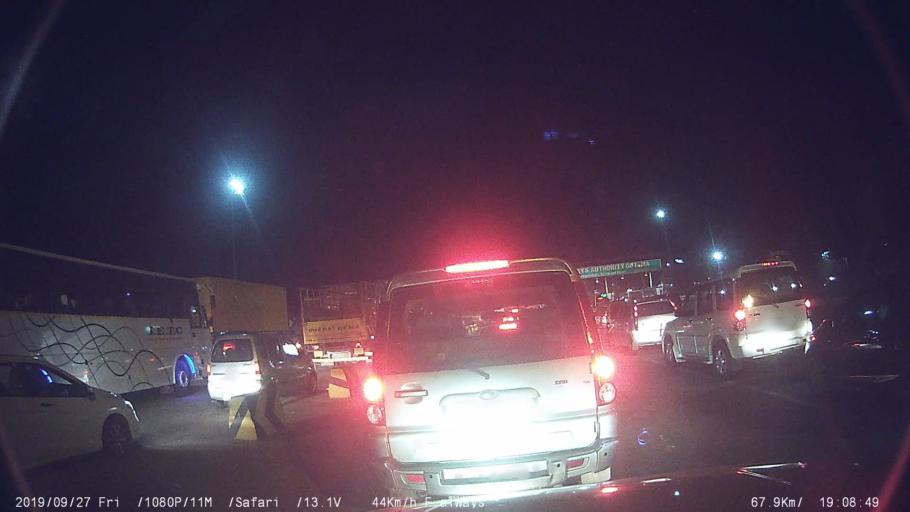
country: IN
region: Tamil Nadu
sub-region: Krishnagiri
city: Krishnagiri
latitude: 12.5651
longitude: 78.1782
